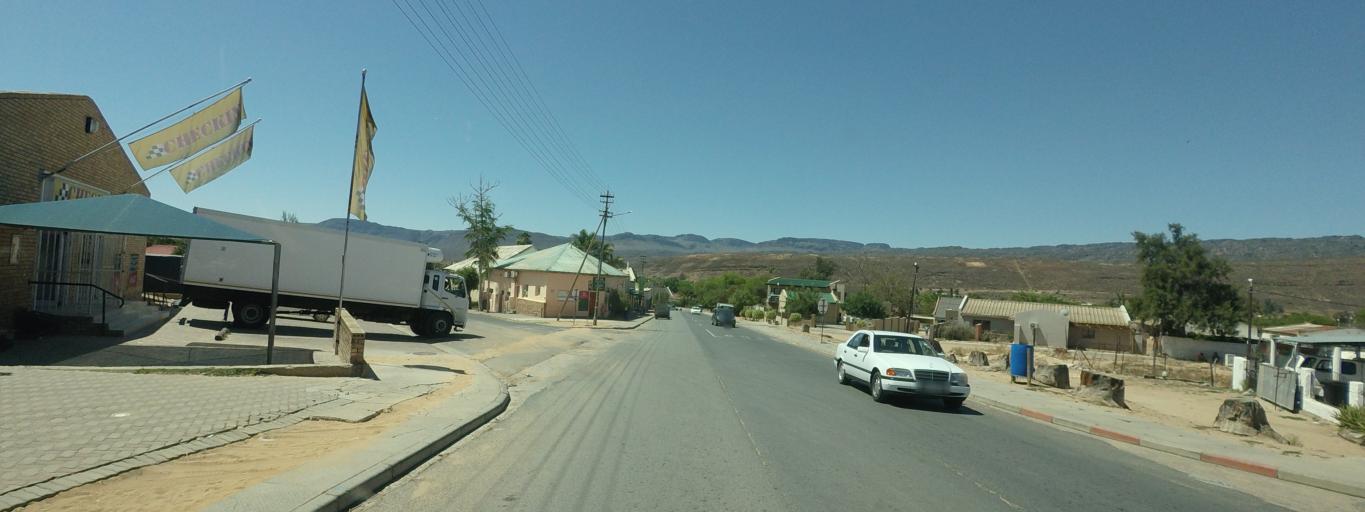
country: ZA
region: Western Cape
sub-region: West Coast District Municipality
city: Clanwilliam
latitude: -32.1828
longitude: 18.8926
